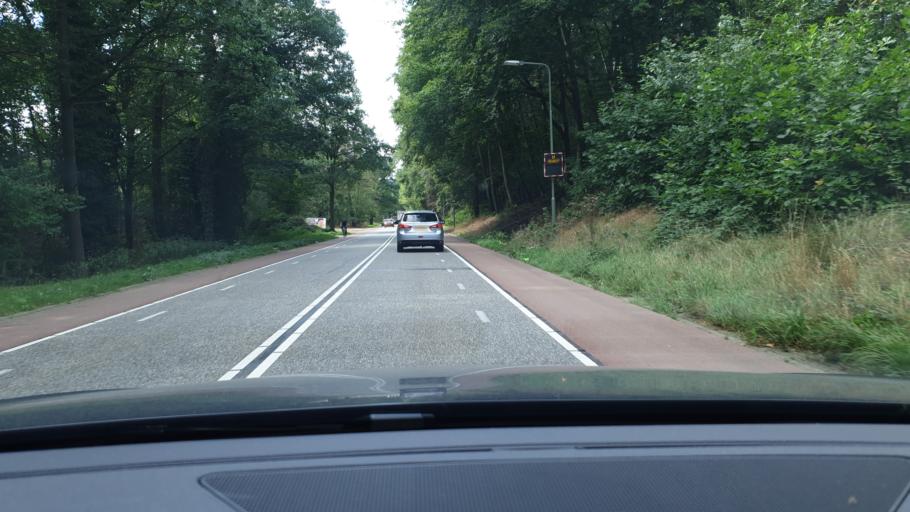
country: NL
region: North Brabant
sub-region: Gemeente Cuijk
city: Cuijk
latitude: 51.7565
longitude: 5.8910
